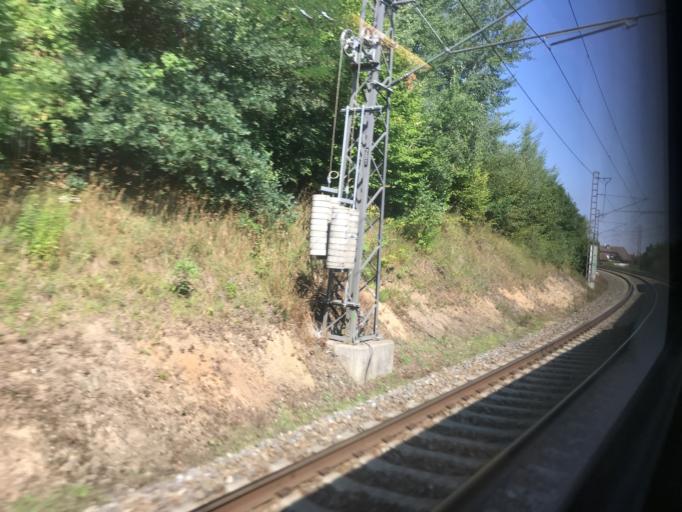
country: CZ
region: Central Bohemia
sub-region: Okres Praha-Vychod
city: Mnichovice
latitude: 49.9428
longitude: 14.6991
